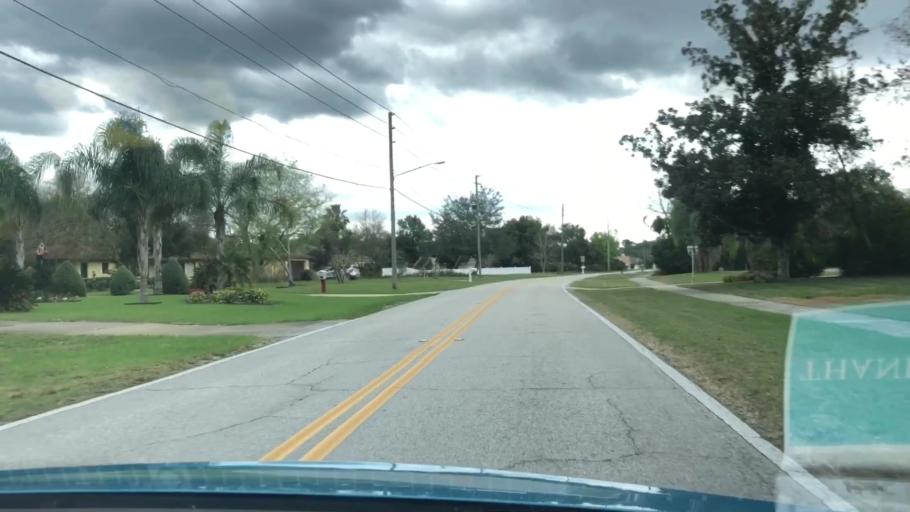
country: US
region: Florida
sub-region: Volusia County
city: Deltona
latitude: 28.8795
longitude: -81.2208
